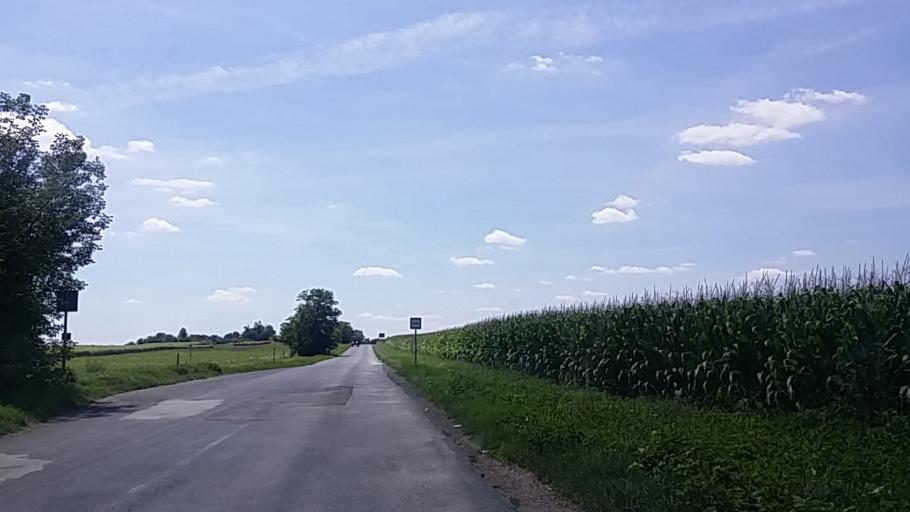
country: HU
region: Fejer
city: Deg
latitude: 46.8676
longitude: 18.4121
